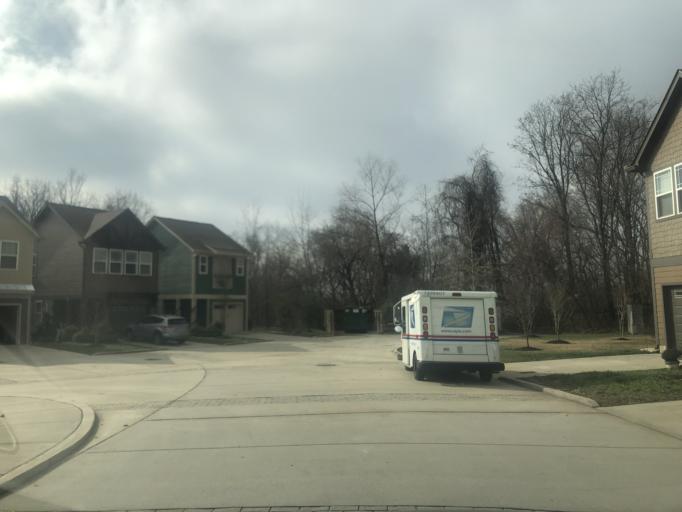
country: US
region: Tennessee
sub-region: Rutherford County
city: La Vergne
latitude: 36.0816
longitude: -86.6505
